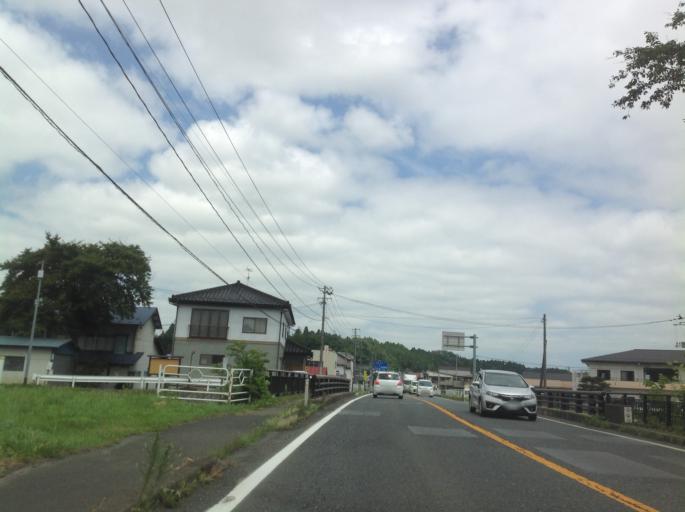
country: JP
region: Iwate
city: Mizusawa
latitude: 39.0926
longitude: 141.1347
